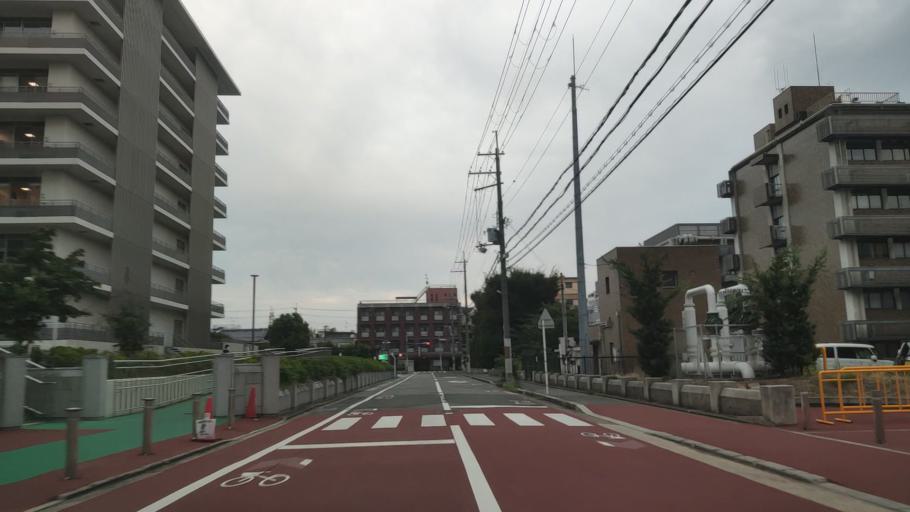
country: JP
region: Kyoto
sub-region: Kyoto-shi
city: Kamigyo-ku
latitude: 35.0197
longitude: 135.7759
